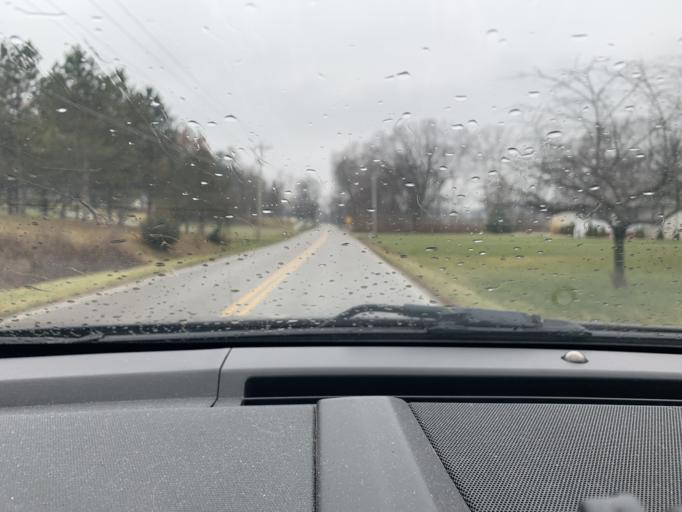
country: US
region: Ohio
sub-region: Ross County
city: Chillicothe
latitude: 39.3843
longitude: -82.9546
